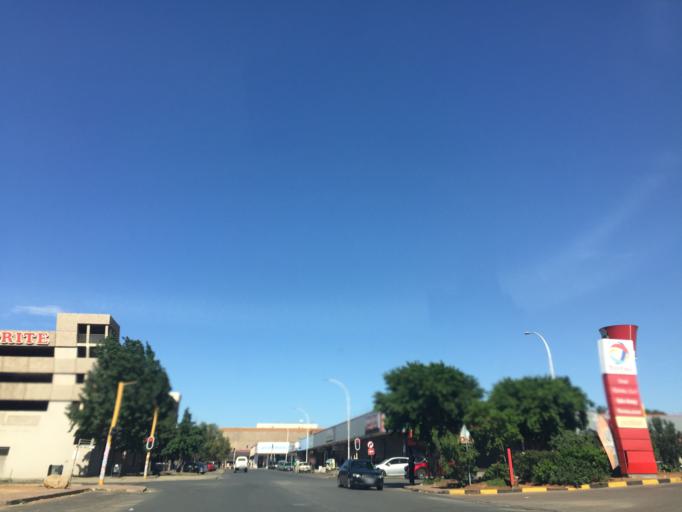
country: ZA
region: Gauteng
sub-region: Sedibeng District Municipality
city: Vanderbijlpark
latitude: -26.6977
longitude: 27.8394
